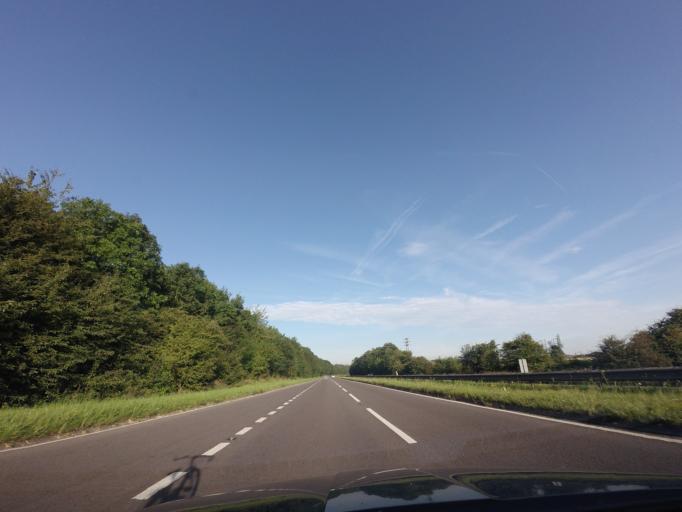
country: GB
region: England
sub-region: Derbyshire
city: Chesterfield
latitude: 53.2109
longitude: -1.3852
